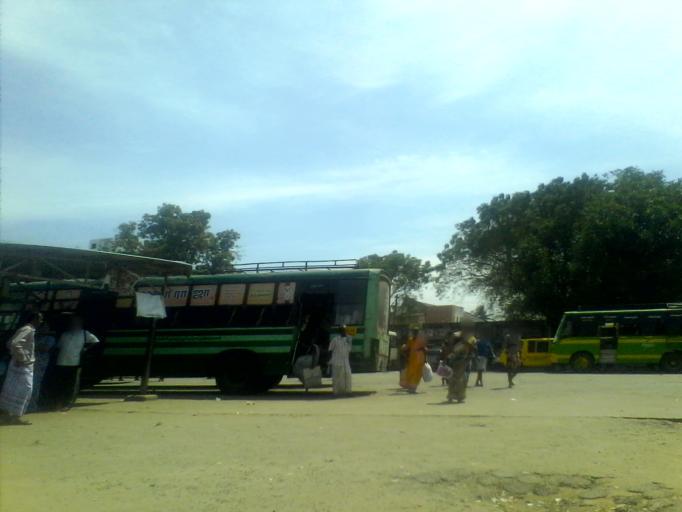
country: IN
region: Tamil Nadu
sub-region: Nagapattinam
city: Mayiladuthurai
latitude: 11.0998
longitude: 79.6510
